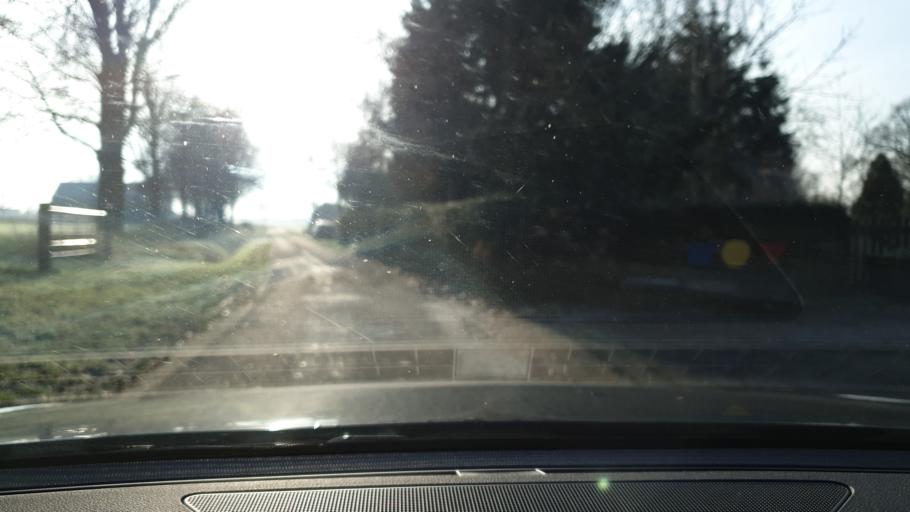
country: NL
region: Limburg
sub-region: Gemeente Peel en Maas
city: Maasbree
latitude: 51.4312
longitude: 6.0480
